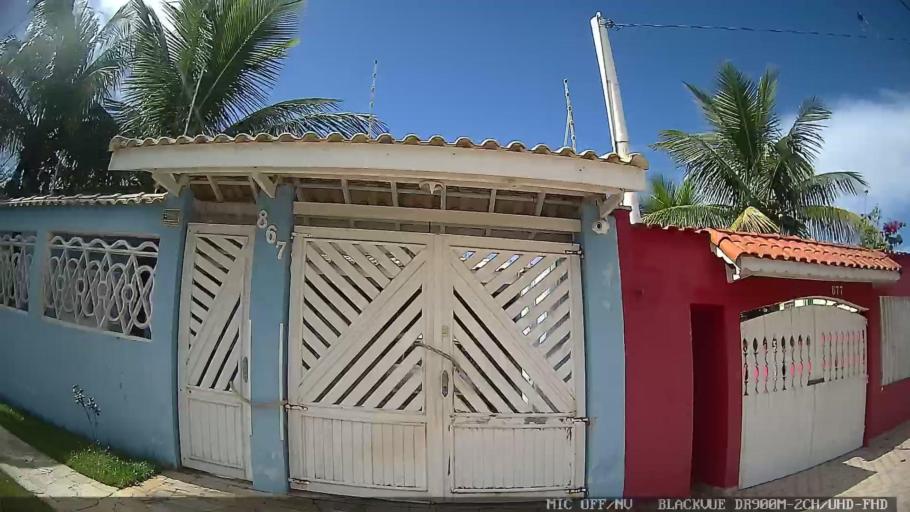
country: BR
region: Sao Paulo
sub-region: Itanhaem
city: Itanhaem
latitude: -24.2469
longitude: -46.8924
